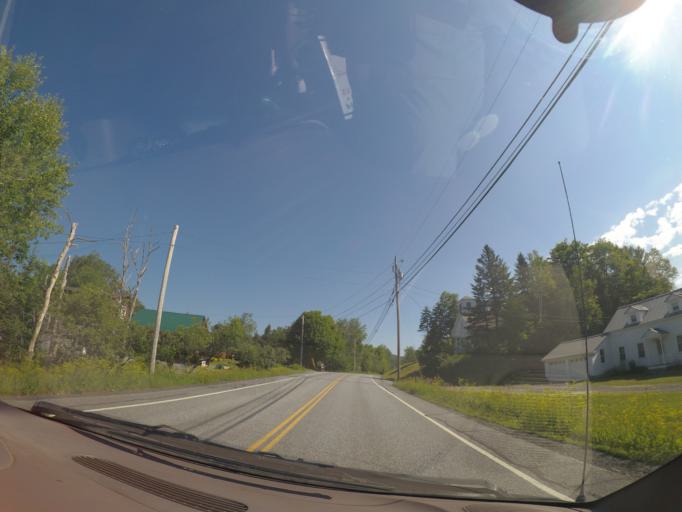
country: US
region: Vermont
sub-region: Bennington County
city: Bennington
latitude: 42.8796
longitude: -73.0798
